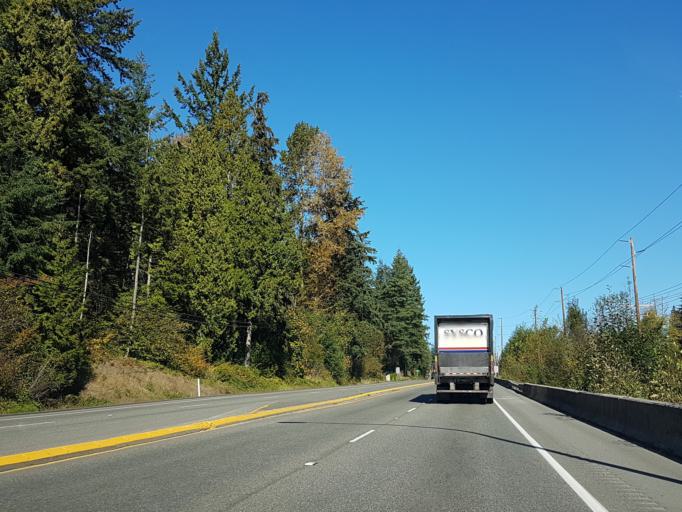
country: US
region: Washington
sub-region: Snohomish County
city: Maltby
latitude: 47.7993
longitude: -122.1433
